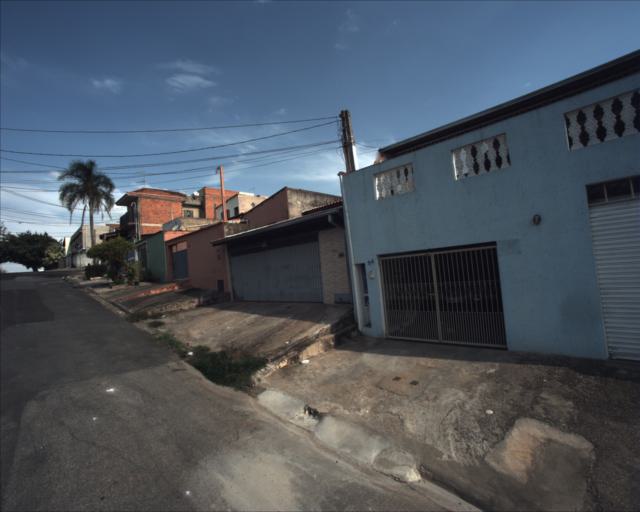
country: BR
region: Sao Paulo
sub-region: Sorocaba
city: Sorocaba
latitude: -23.4927
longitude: -47.5217
